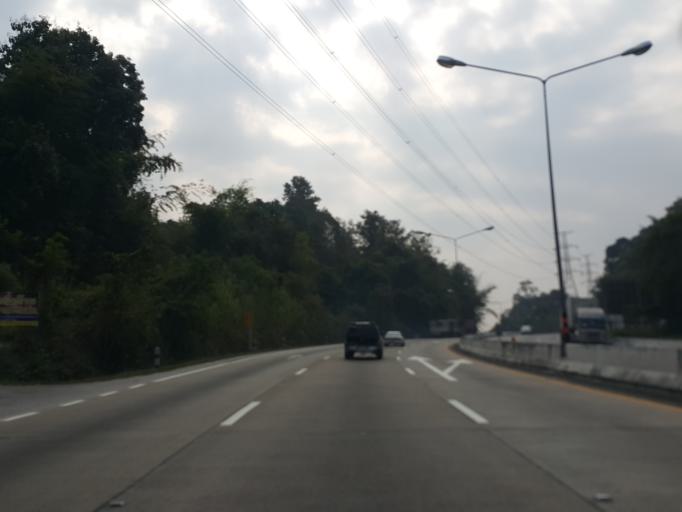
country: TH
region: Lamphun
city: Mae Tha
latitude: 18.4285
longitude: 99.2079
